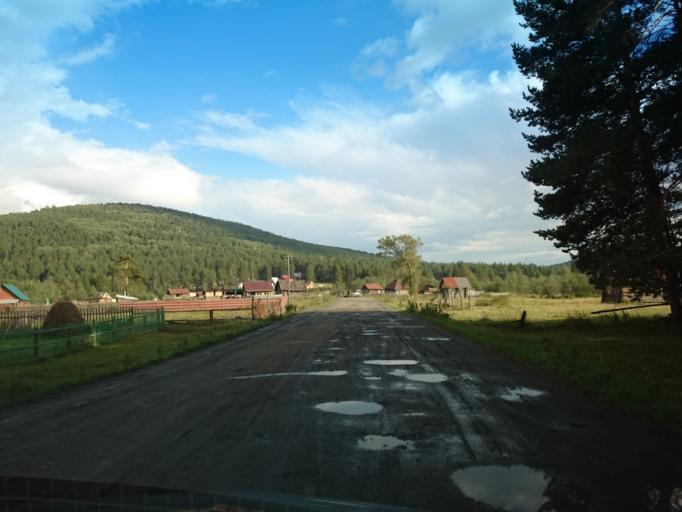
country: RU
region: Bashkortostan
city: Beloretsk
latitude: 54.0487
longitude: 58.3266
